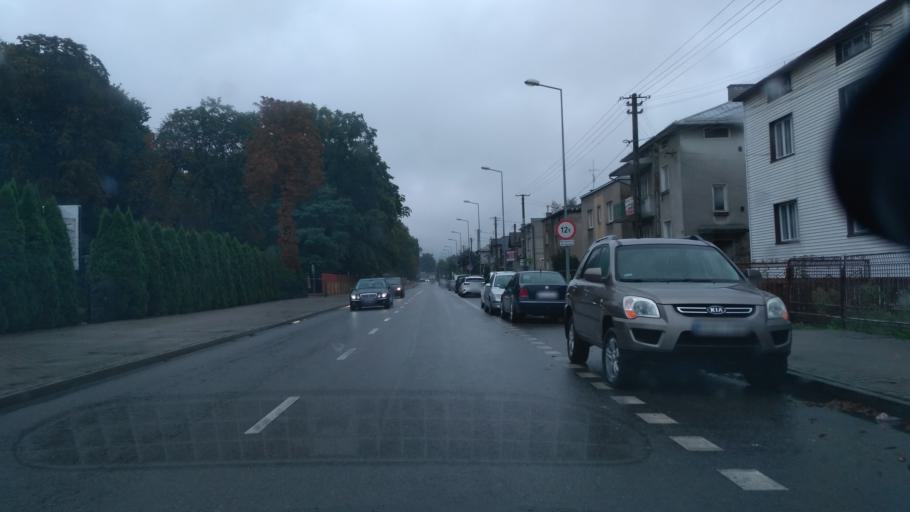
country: PL
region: Subcarpathian Voivodeship
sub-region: Powiat debicki
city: Debica
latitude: 50.0616
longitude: 21.4059
